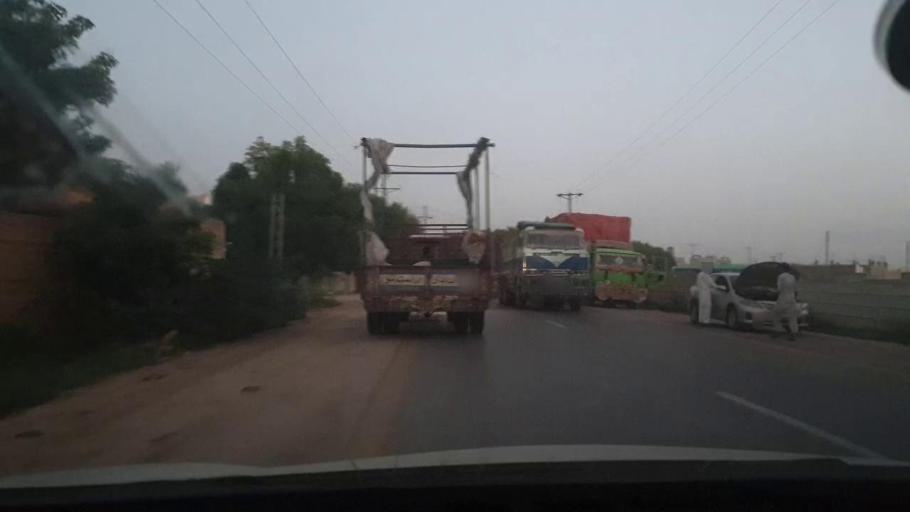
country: PK
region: Sindh
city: Tando Adam
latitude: 25.7508
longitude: 68.6441
